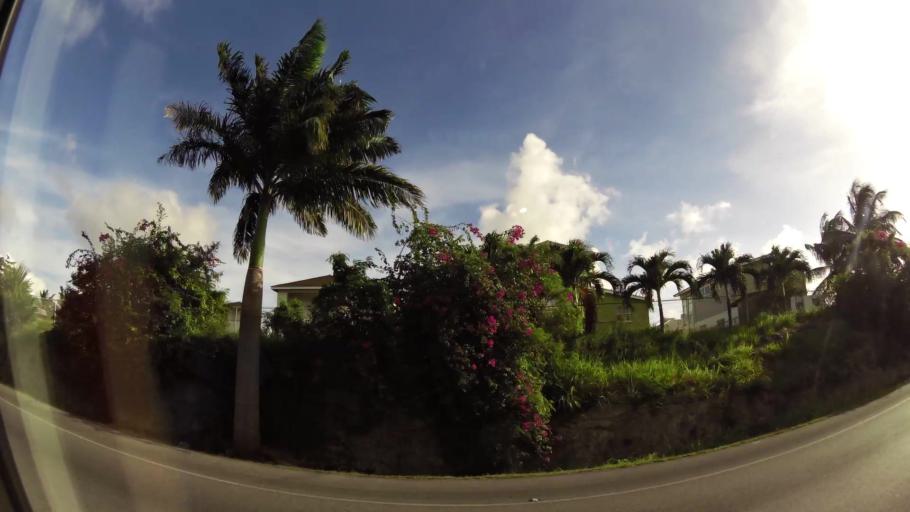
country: BB
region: Christ Church
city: Oistins
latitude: 13.0778
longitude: -59.5605
